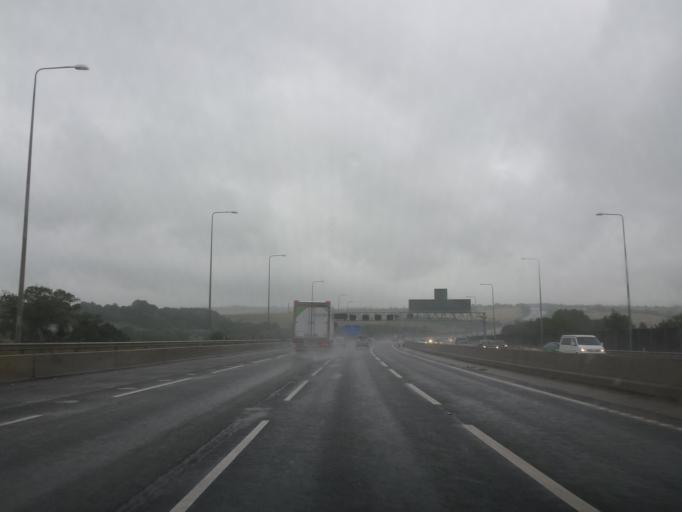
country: GB
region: England
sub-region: Derbyshire
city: Pinxton
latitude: 53.0967
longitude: -1.3135
